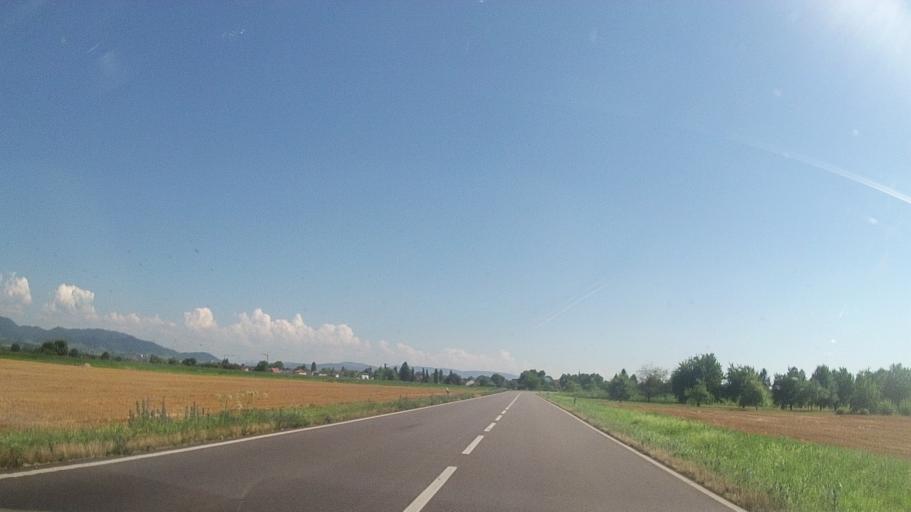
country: DE
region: Baden-Wuerttemberg
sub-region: Freiburg Region
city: Willstatt
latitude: 48.5167
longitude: 7.9256
